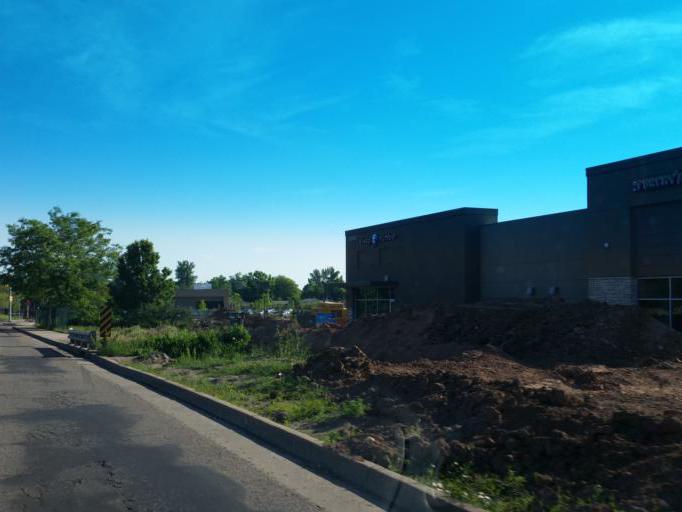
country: US
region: Colorado
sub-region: Larimer County
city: Fort Collins
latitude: 40.5421
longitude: -105.0769
